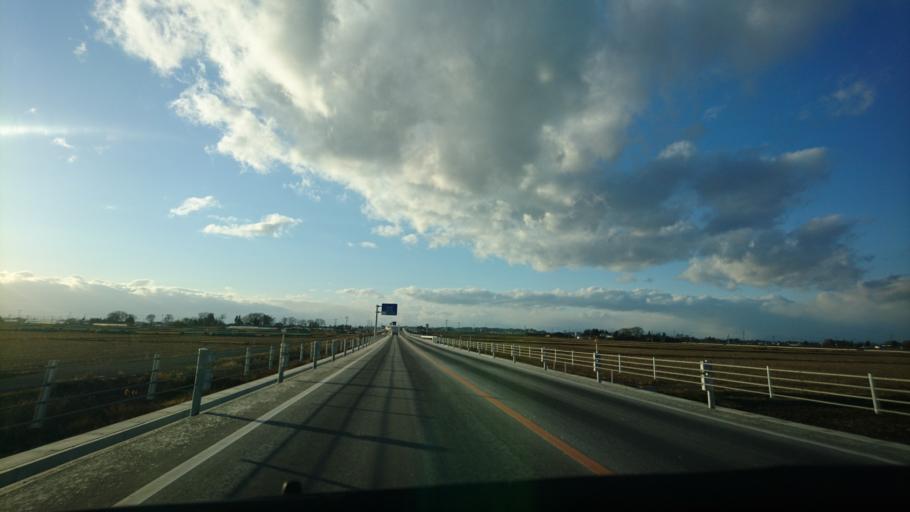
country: JP
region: Miyagi
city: Wakuya
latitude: 38.6855
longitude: 141.2437
